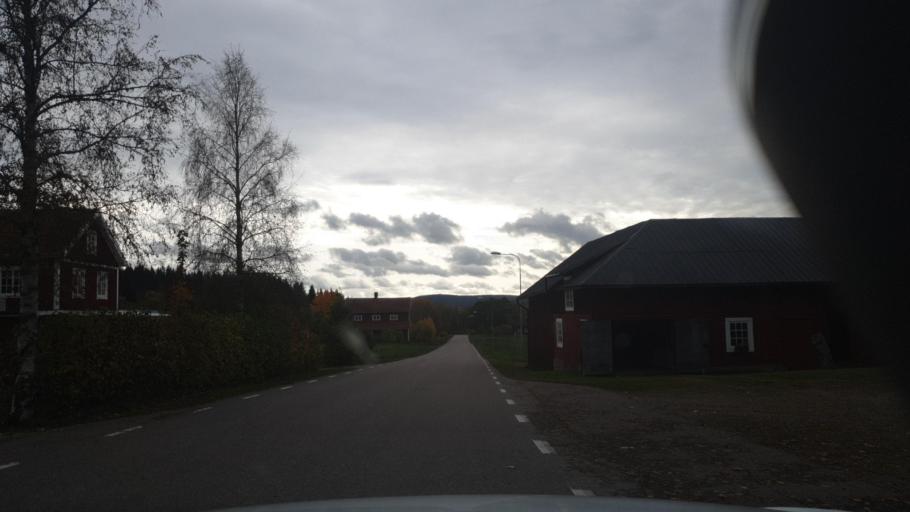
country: SE
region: Vaermland
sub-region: Arvika Kommun
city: Arvika
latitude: 59.7642
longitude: 12.7936
